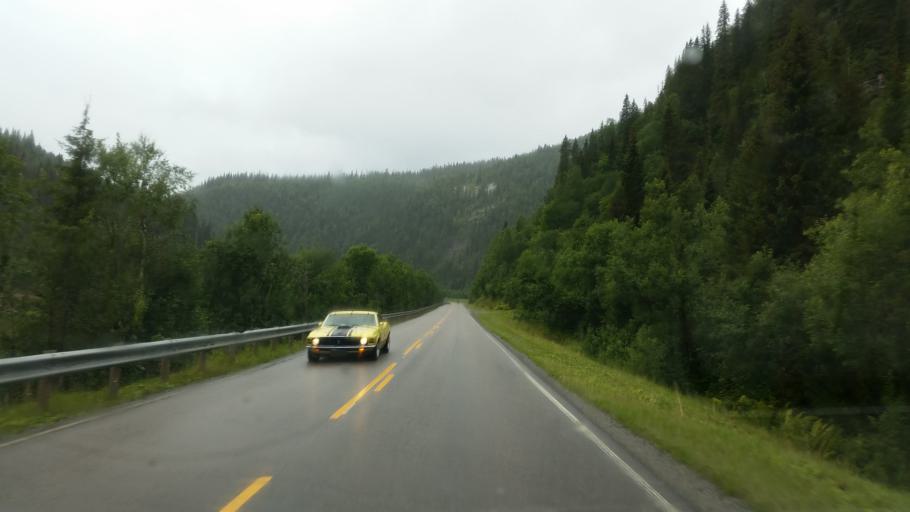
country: NO
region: Nordland
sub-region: Rana
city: Mo i Rana
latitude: 66.4026
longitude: 14.4143
